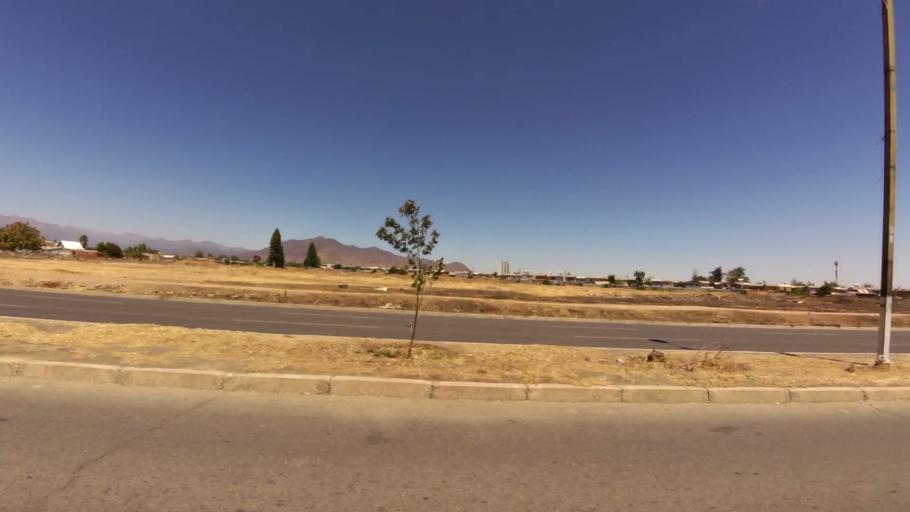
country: CL
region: O'Higgins
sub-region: Provincia de Cachapoal
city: Rancagua
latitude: -34.1622
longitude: -70.7092
